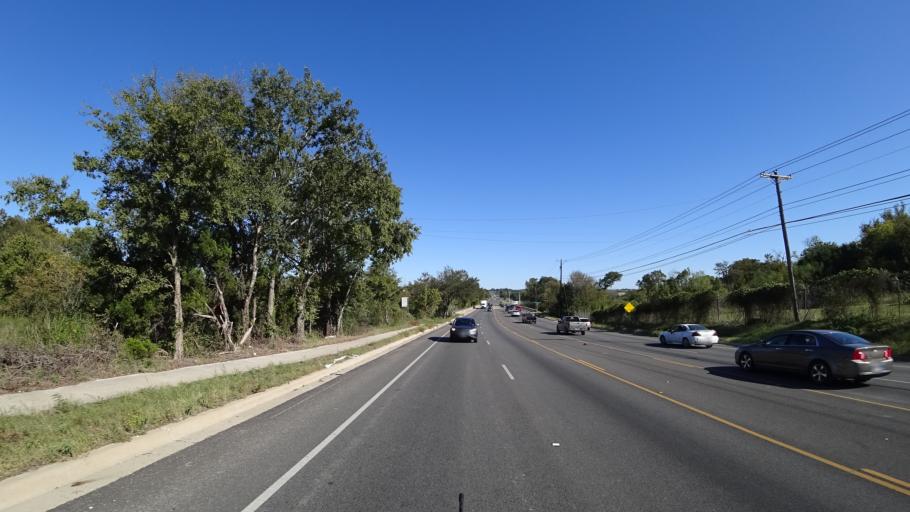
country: US
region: Texas
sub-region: Travis County
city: Hornsby Bend
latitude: 30.2841
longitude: -97.6566
